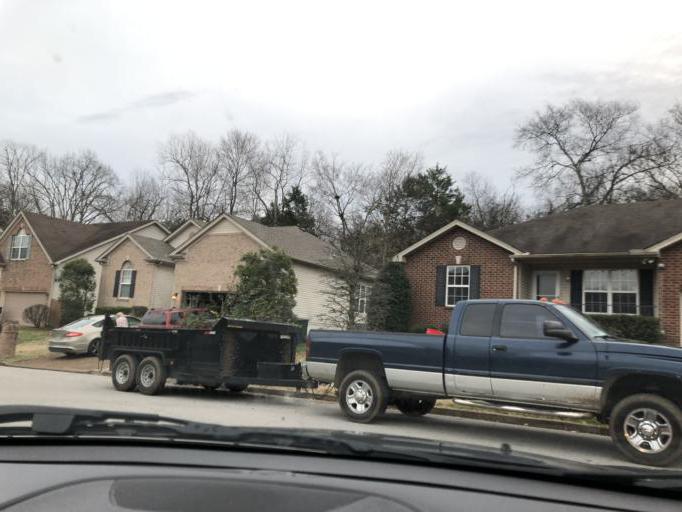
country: US
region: Tennessee
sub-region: Wilson County
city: Green Hill
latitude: 36.1995
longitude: -86.5954
